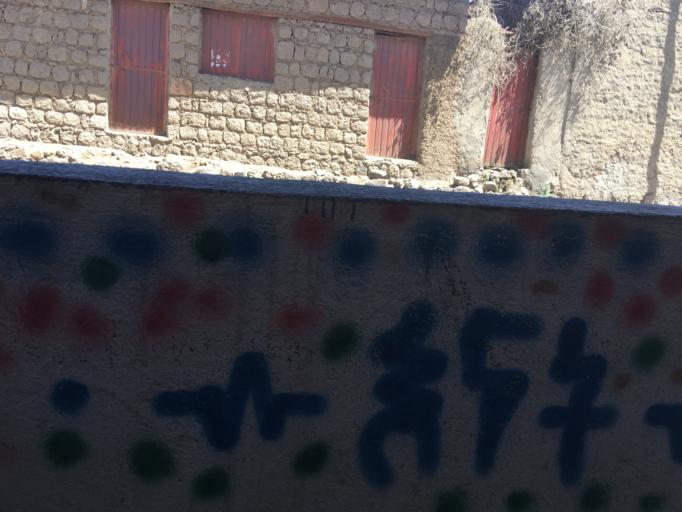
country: ET
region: Tigray
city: Korem
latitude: 12.6258
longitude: 39.0344
